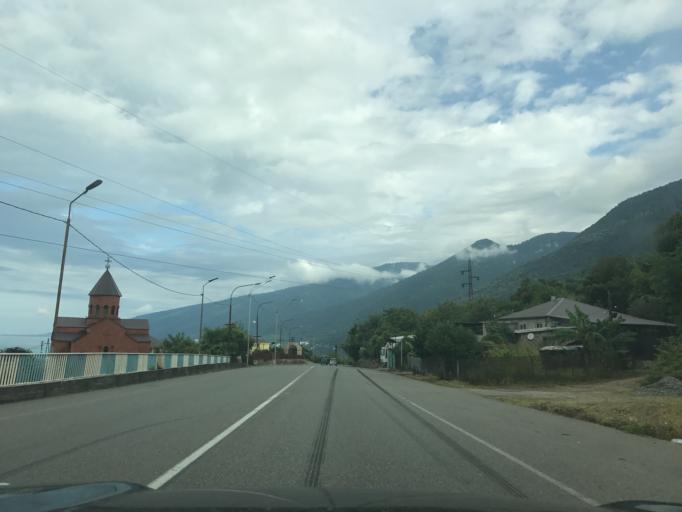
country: GE
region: Abkhazia
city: Gagra
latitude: 43.2939
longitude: 40.2660
